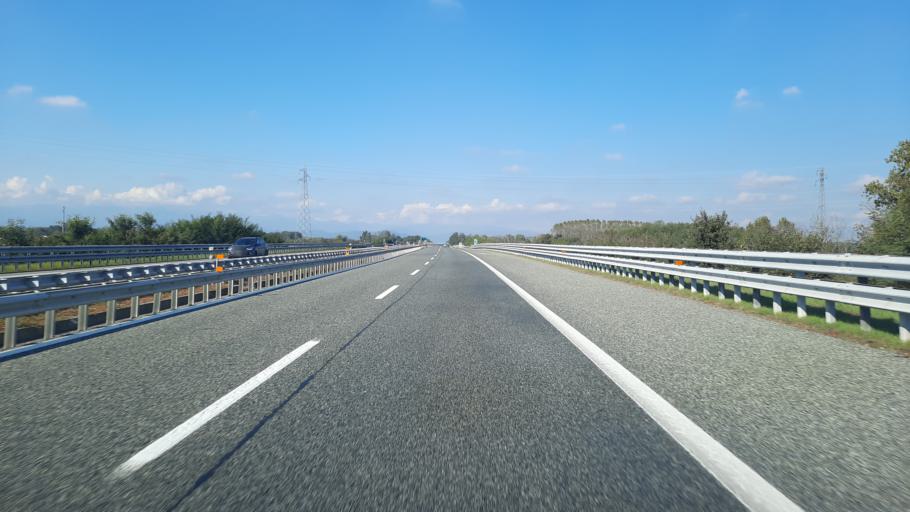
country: IT
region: Piedmont
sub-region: Provincia di Novara
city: Carpignano Sesia
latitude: 45.5375
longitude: 8.4299
